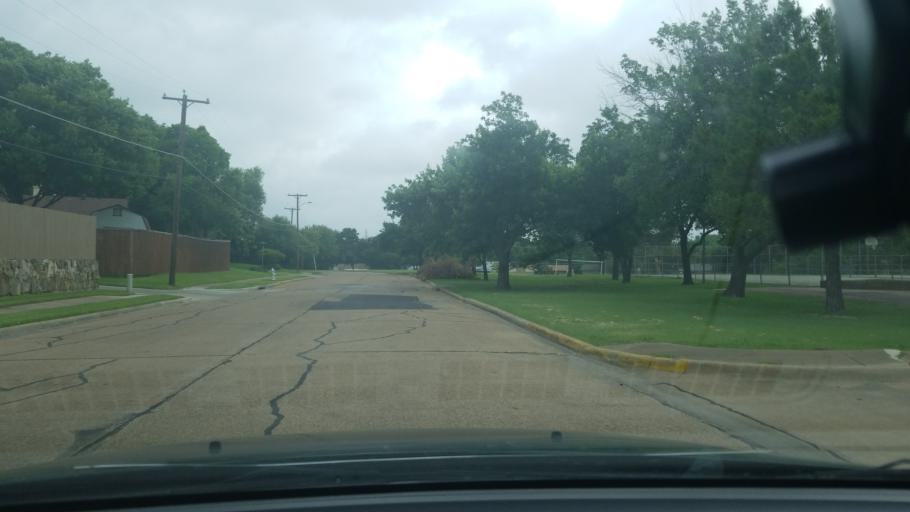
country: US
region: Texas
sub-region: Dallas County
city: Mesquite
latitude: 32.7850
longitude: -96.6398
